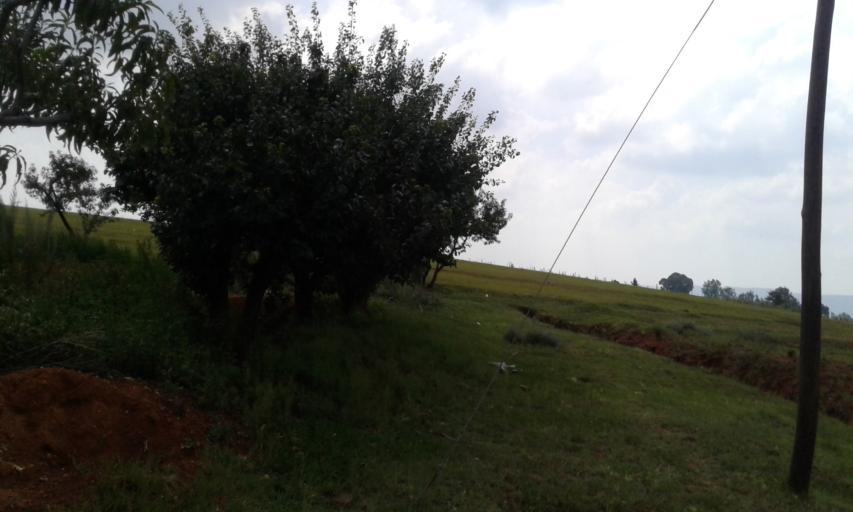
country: LS
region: Maseru
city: Maseru
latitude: -29.4311
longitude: 27.5748
